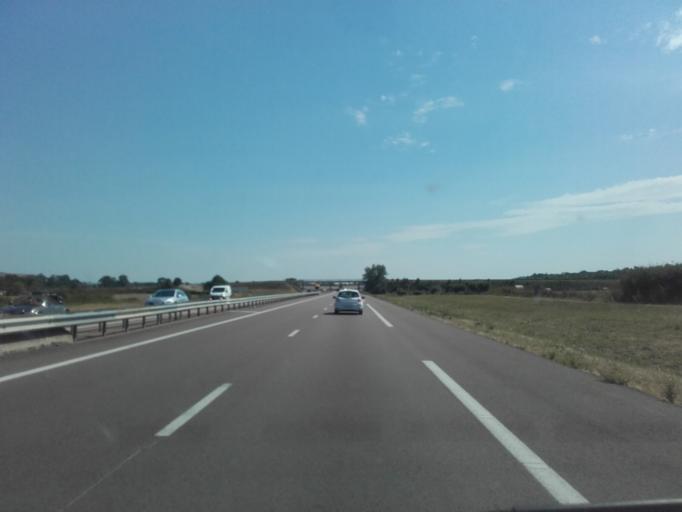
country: FR
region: Bourgogne
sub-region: Departement de la Cote-d'Or
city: Pouilly-en-Auxois
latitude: 47.2776
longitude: 4.5105
